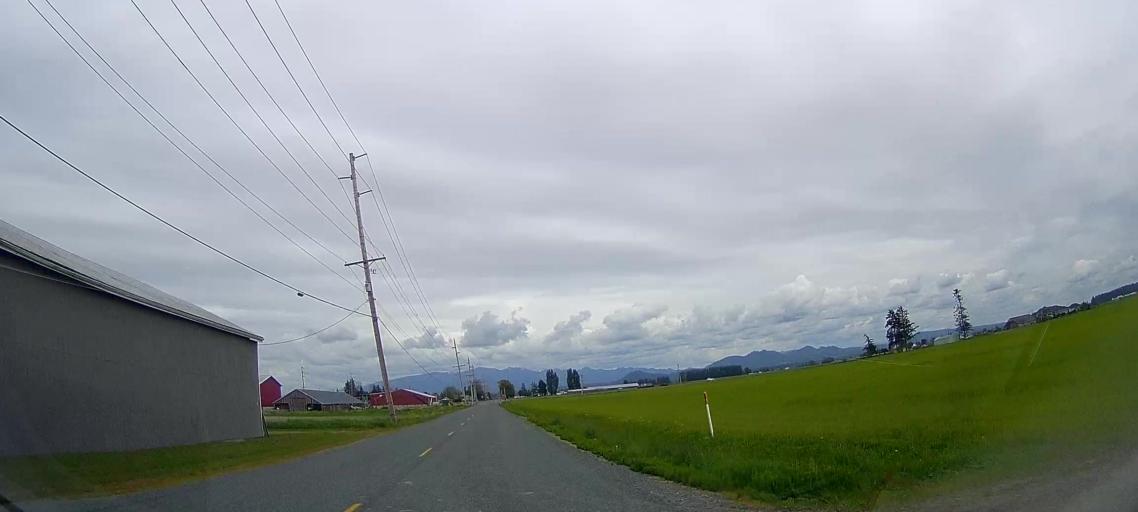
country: US
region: Washington
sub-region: Skagit County
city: Mount Vernon
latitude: 48.4209
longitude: -122.4759
